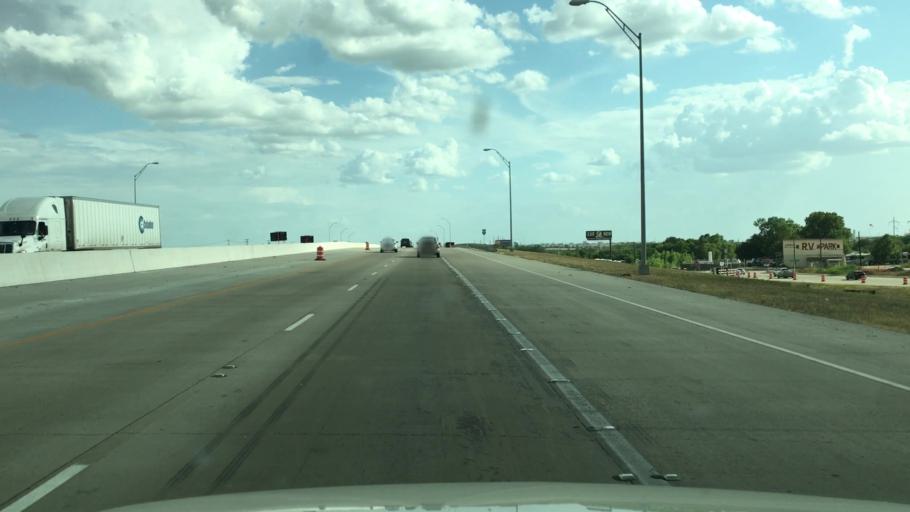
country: US
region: Texas
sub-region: Bell County
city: Troy
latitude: 31.1570
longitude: -97.3235
